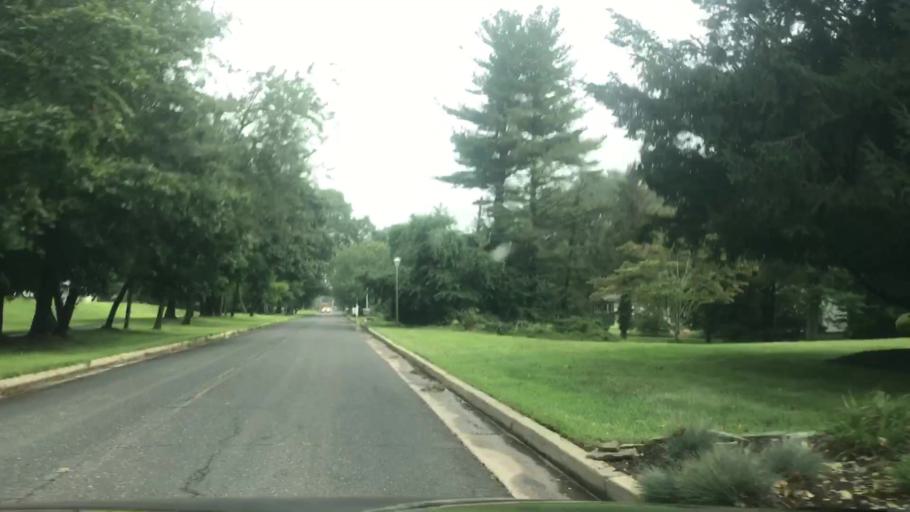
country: US
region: New Jersey
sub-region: Monmouth County
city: Fair Haven
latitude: 40.3491
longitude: -74.0418
